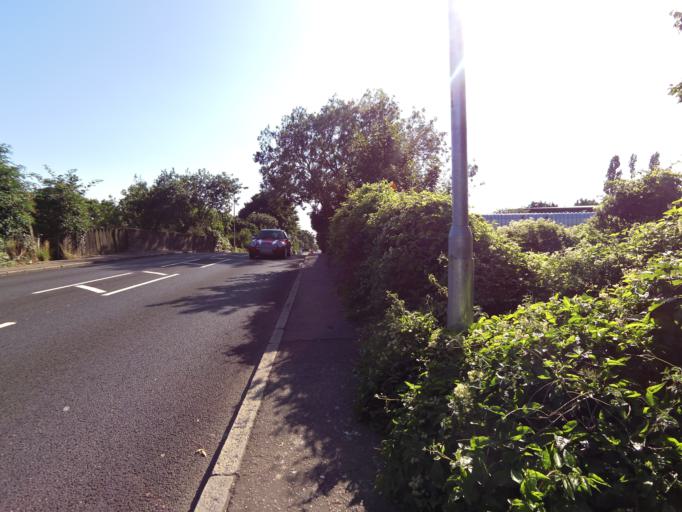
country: GB
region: England
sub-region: Essex
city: Witham
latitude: 51.8044
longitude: 0.6463
